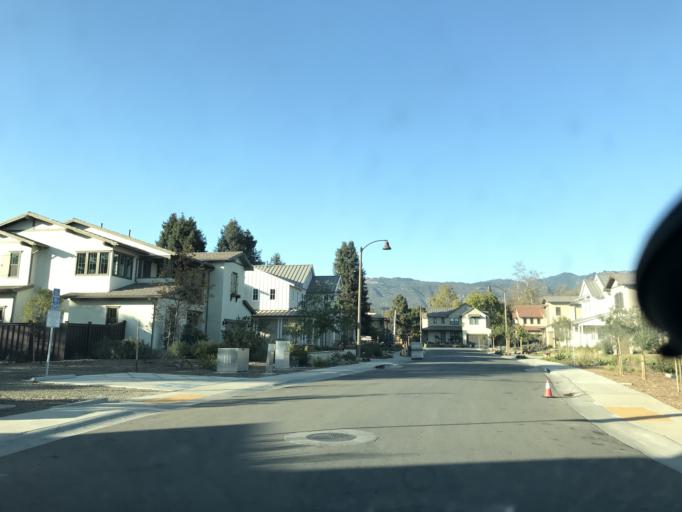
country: US
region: California
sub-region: Santa Barbara County
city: Goleta
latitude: 34.4499
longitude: -119.8138
